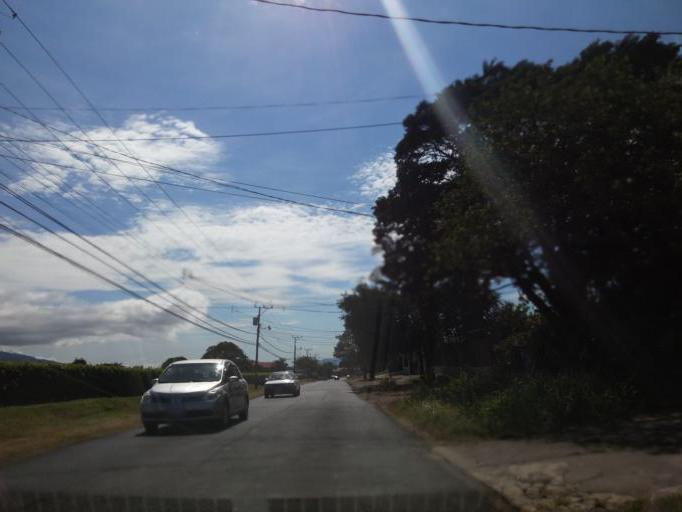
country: CR
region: Heredia
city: Santo Domingo
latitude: 10.0333
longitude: -84.1652
